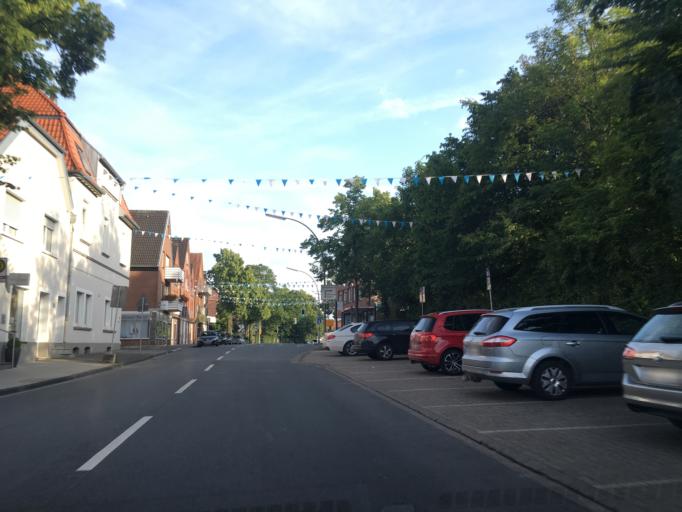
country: DE
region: North Rhine-Westphalia
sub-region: Regierungsbezirk Munster
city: Muenster
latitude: 51.9552
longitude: 7.5323
